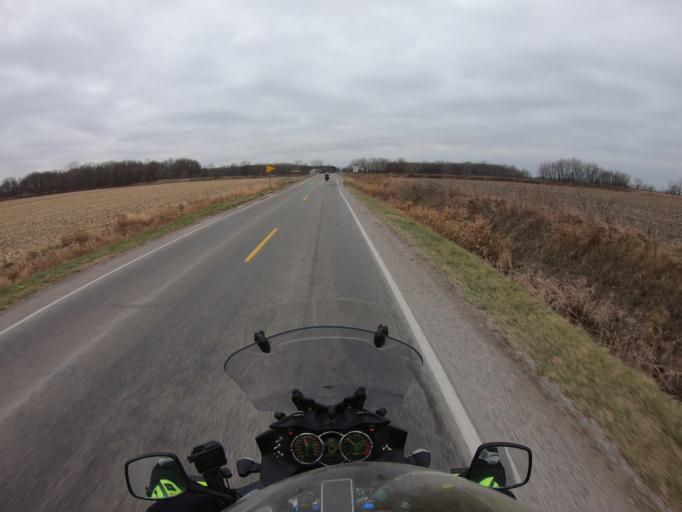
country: US
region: Michigan
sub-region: Saginaw County
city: Burt
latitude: 43.2562
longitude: -84.0038
